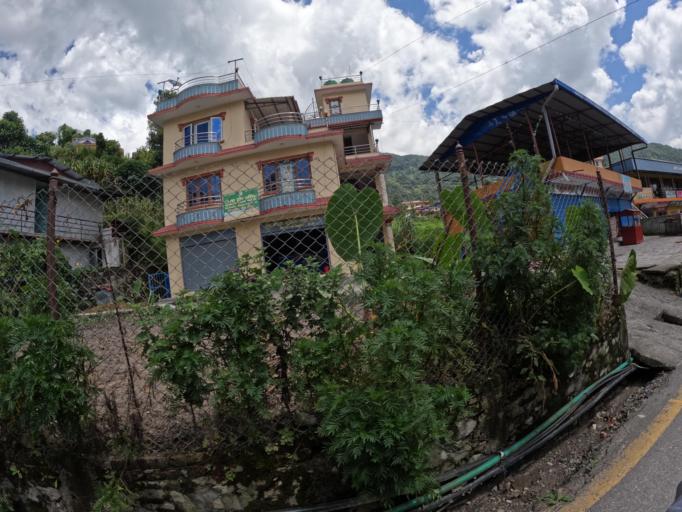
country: NP
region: Central Region
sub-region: Bagmati Zone
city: Kathmandu
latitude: 27.7968
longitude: 85.3296
